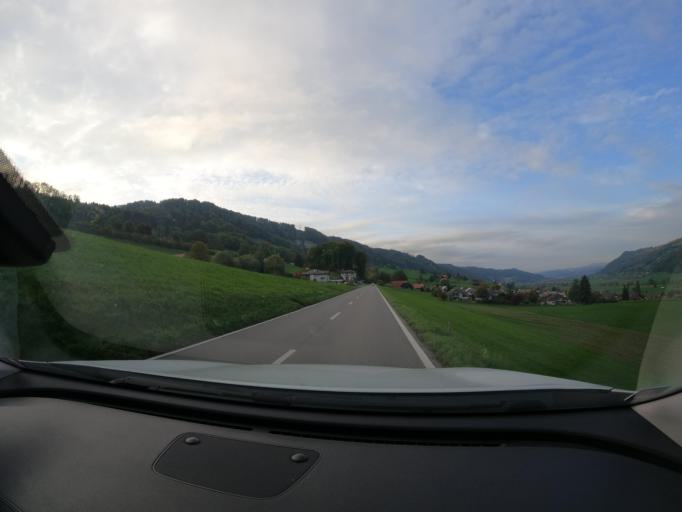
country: CH
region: Bern
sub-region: Bern-Mittelland District
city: Hermiswil
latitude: 46.8344
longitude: 7.4960
